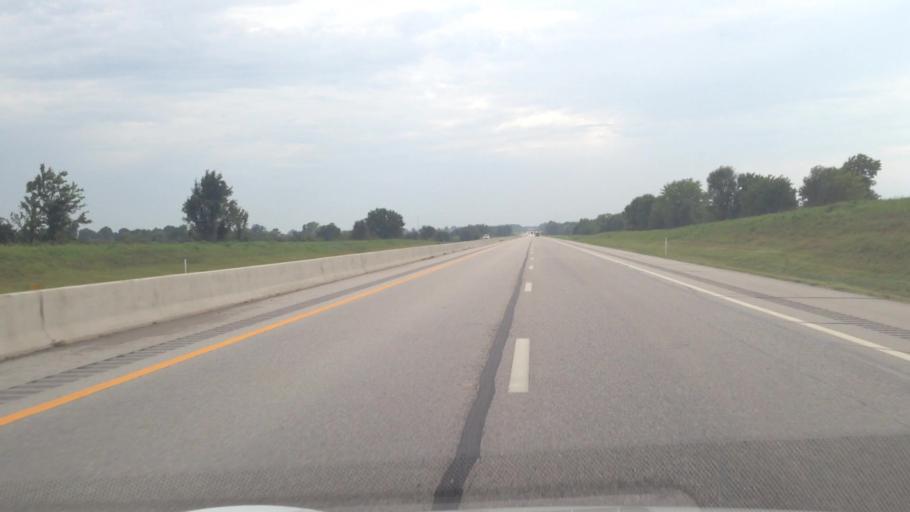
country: US
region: Kansas
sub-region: Cherokee County
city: Baxter Springs
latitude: 36.9667
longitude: -94.6550
